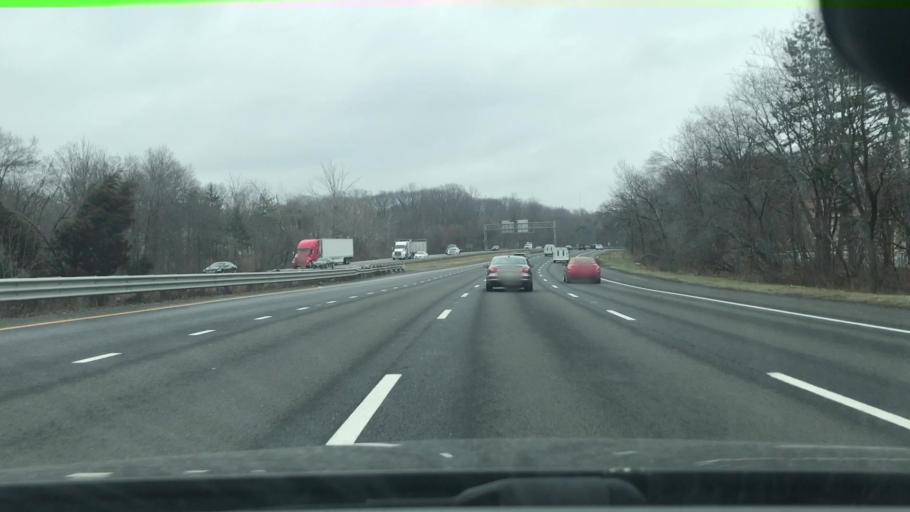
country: US
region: New Jersey
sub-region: Morris County
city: East Hanover
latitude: 40.8616
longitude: -74.3620
